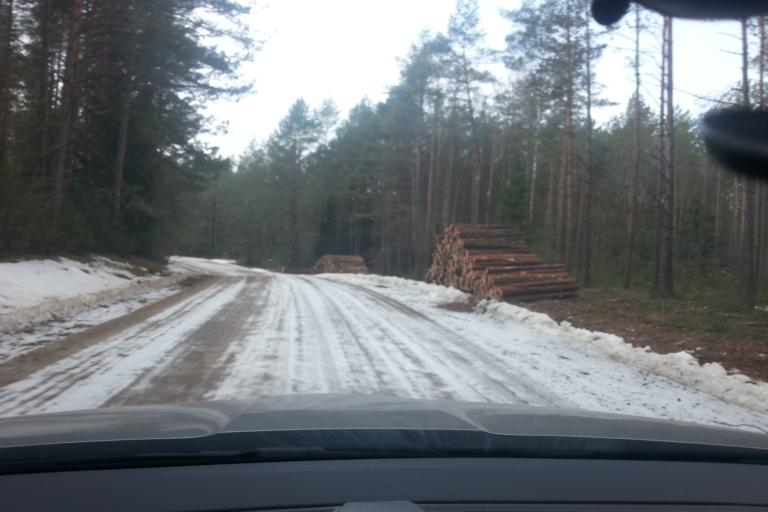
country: LT
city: Trakai
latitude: 54.5281
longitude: 24.9685
